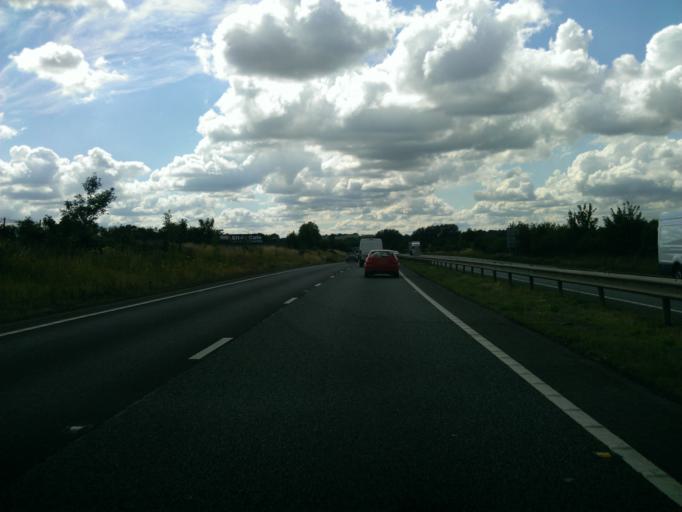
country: GB
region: England
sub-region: Northamptonshire
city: Long Buckby
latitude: 52.3989
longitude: -1.0114
